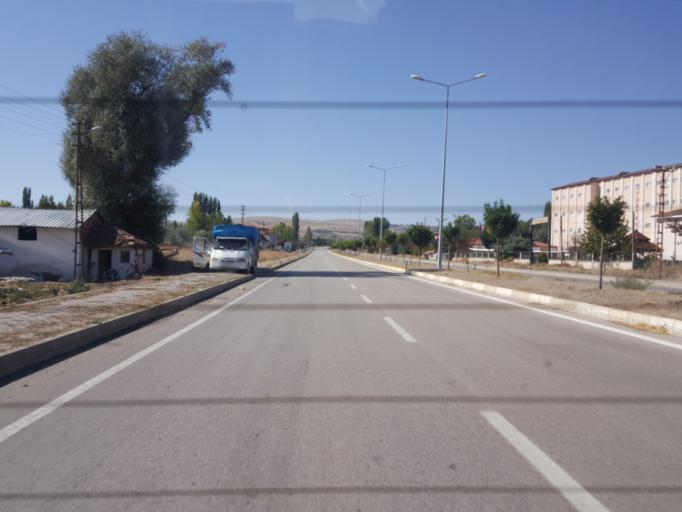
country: TR
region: Tokat
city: Zile
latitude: 40.2848
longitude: 35.8614
